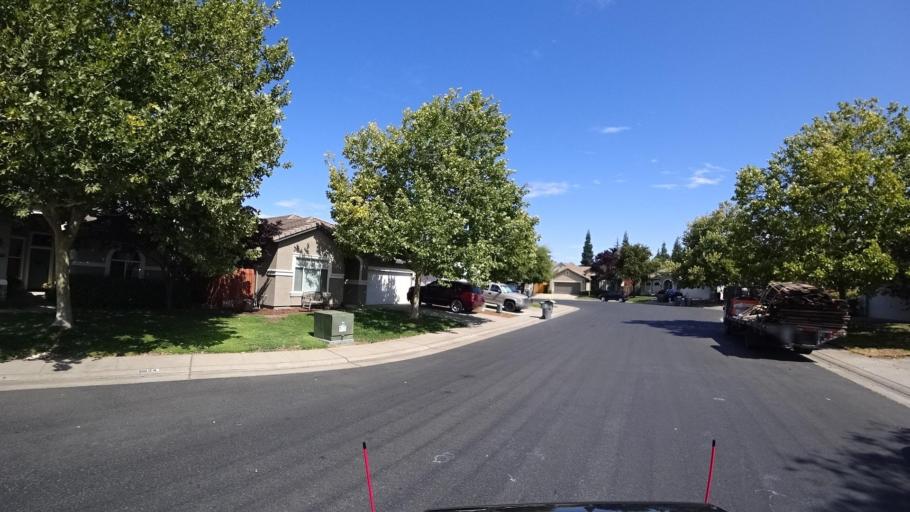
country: US
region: California
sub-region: Placer County
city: Roseville
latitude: 38.7982
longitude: -121.2881
